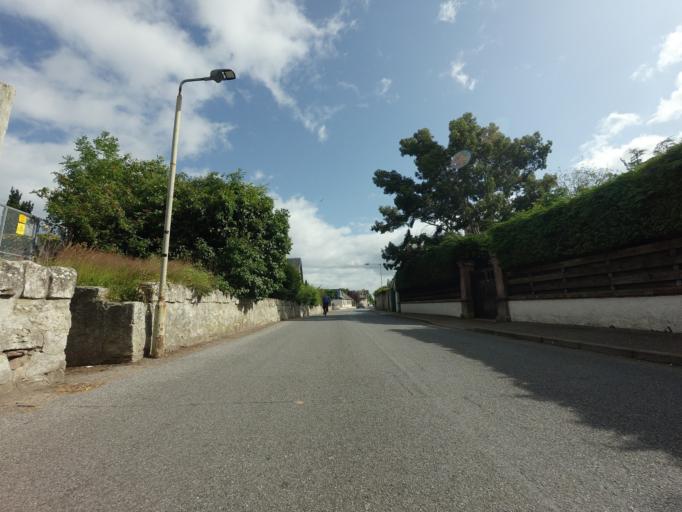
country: GB
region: Scotland
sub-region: Highland
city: Nairn
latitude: 57.5817
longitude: -3.8735
